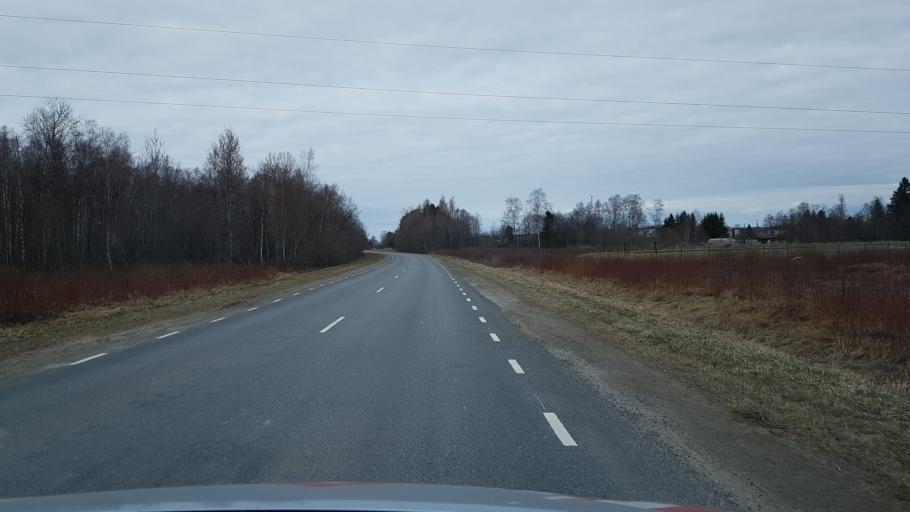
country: EE
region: Ida-Virumaa
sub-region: Sillamaee linn
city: Sillamae
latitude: 59.3651
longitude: 27.7589
